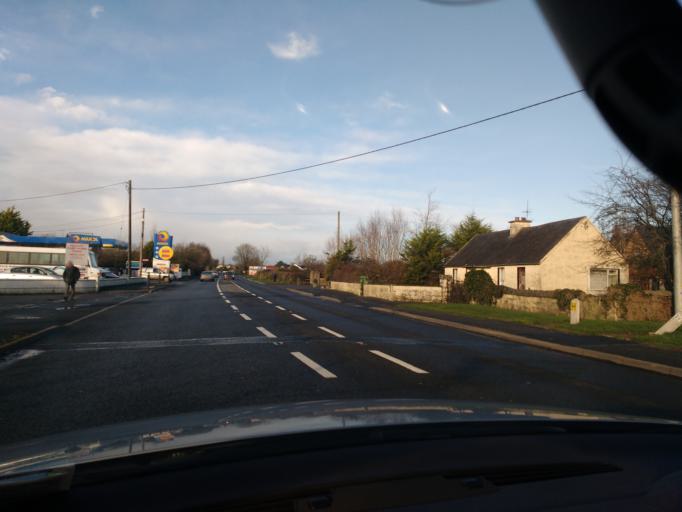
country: IE
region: Munster
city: Thurles
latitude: 52.6656
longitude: -7.8063
